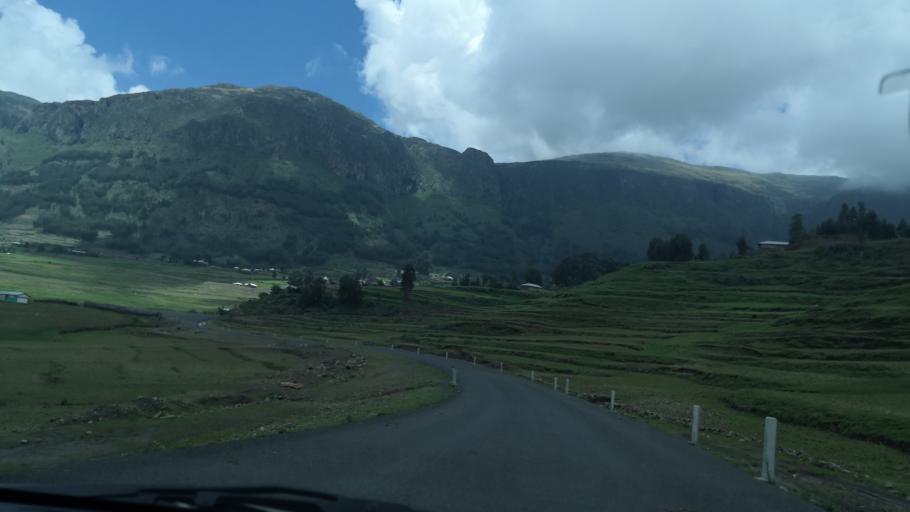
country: ET
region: Amhara
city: Kemise
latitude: 10.3605
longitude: 39.8281
